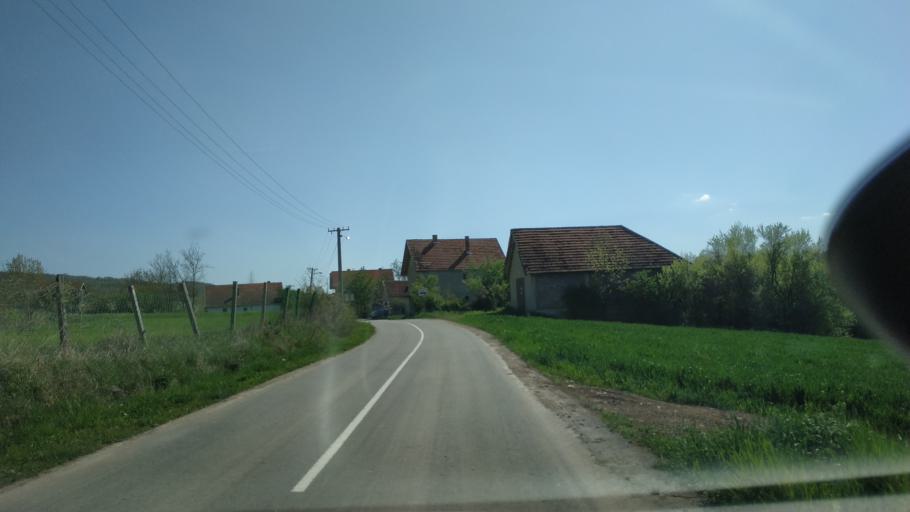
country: RS
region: Central Serbia
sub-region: Nisavski Okrug
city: Nis
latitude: 43.4677
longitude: 21.8630
